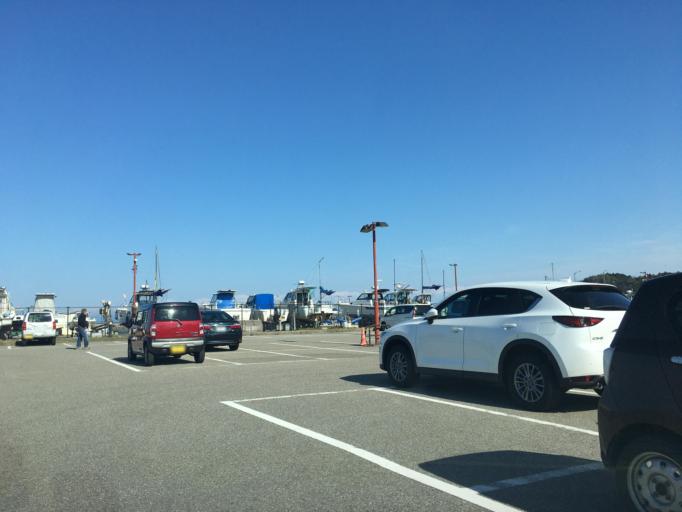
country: JP
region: Toyama
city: Himi
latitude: 36.8213
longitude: 137.0297
